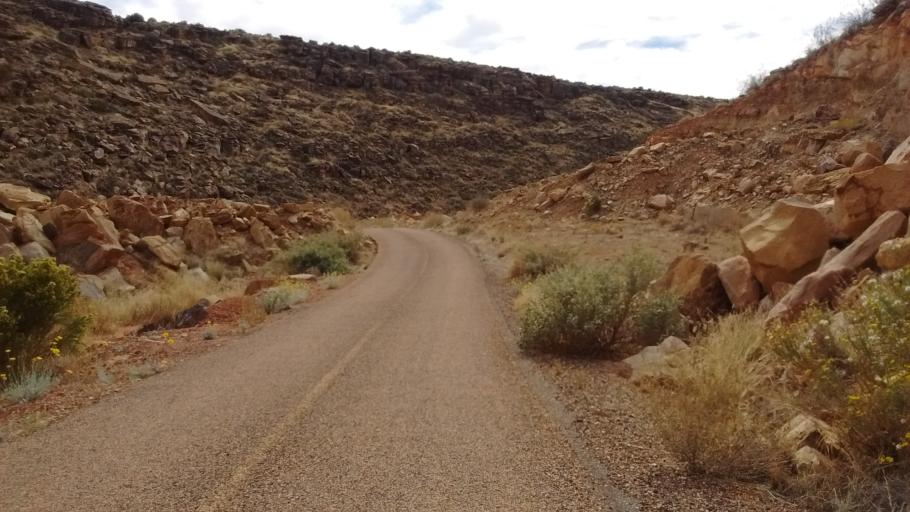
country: US
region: Utah
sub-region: Washington County
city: Washington
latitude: 37.1296
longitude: -113.4728
